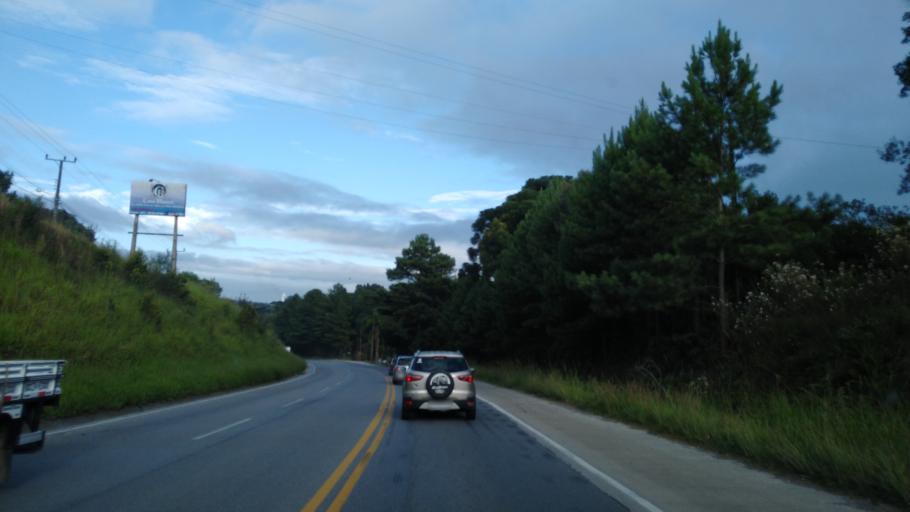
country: BR
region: Santa Catarina
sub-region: Rio Negrinho
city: Rio Negrinho
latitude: -26.2444
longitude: -49.4553
